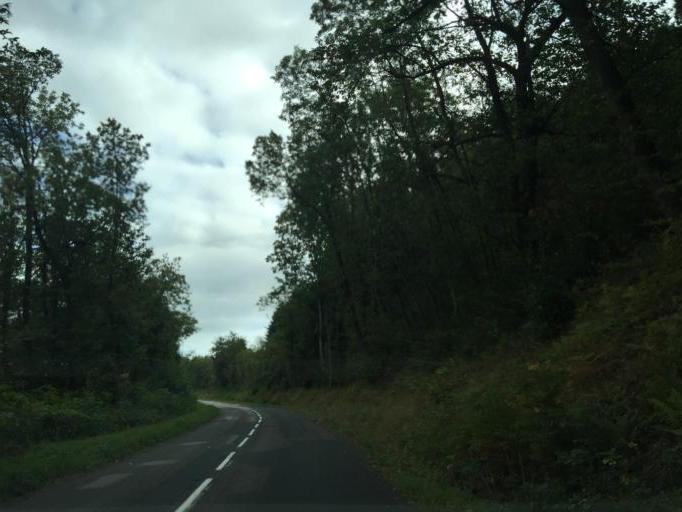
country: FR
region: Rhone-Alpes
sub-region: Departement de la Loire
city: Farnay
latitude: 45.4615
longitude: 4.6343
